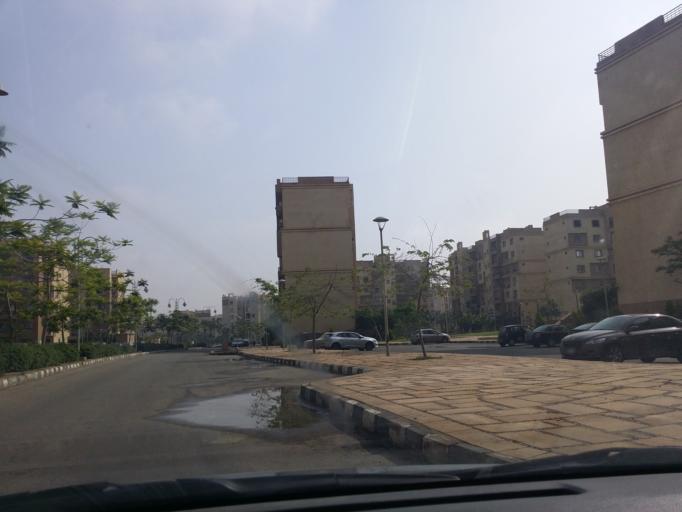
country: EG
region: Muhafazat al Qalyubiyah
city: Al Khankah
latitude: 30.0824
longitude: 31.6452
